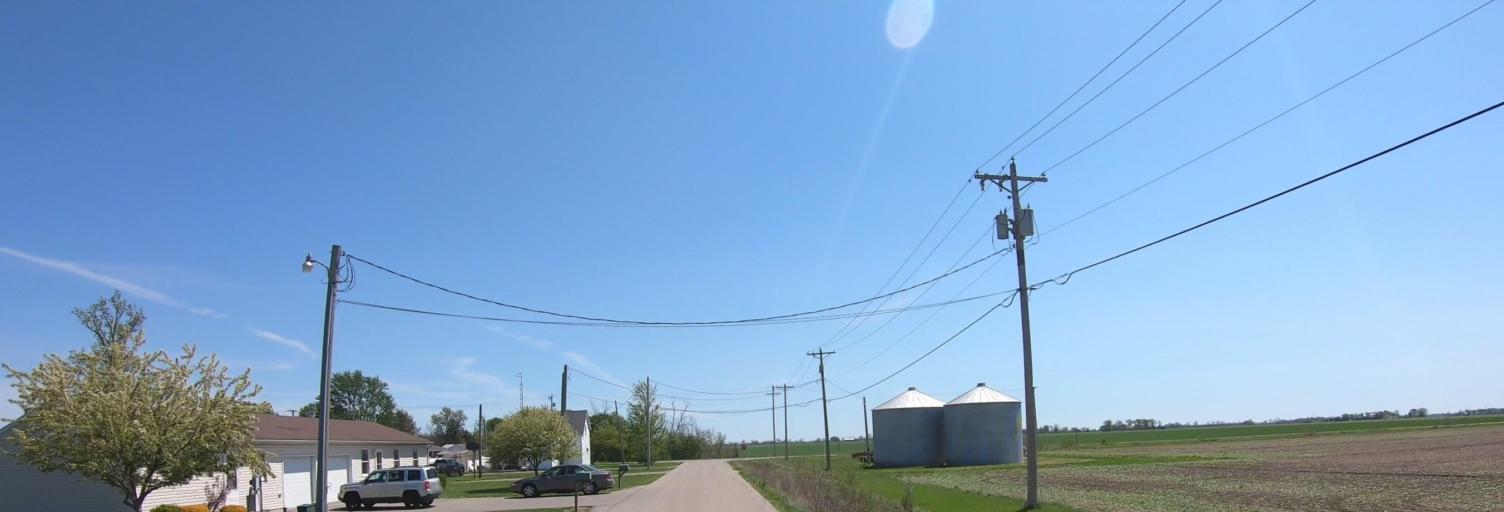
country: US
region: Ohio
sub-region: Henry County
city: Deshler
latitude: 41.2000
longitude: -83.9028
